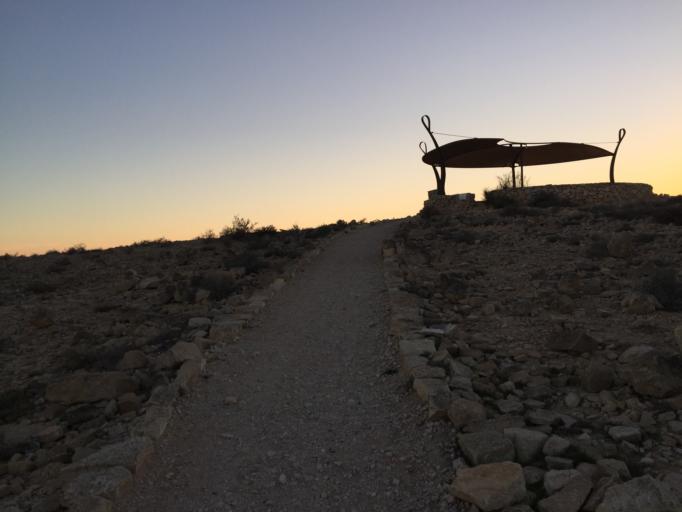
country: IL
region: Southern District
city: Midreshet Ben-Gurion
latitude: 30.8879
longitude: 34.7922
